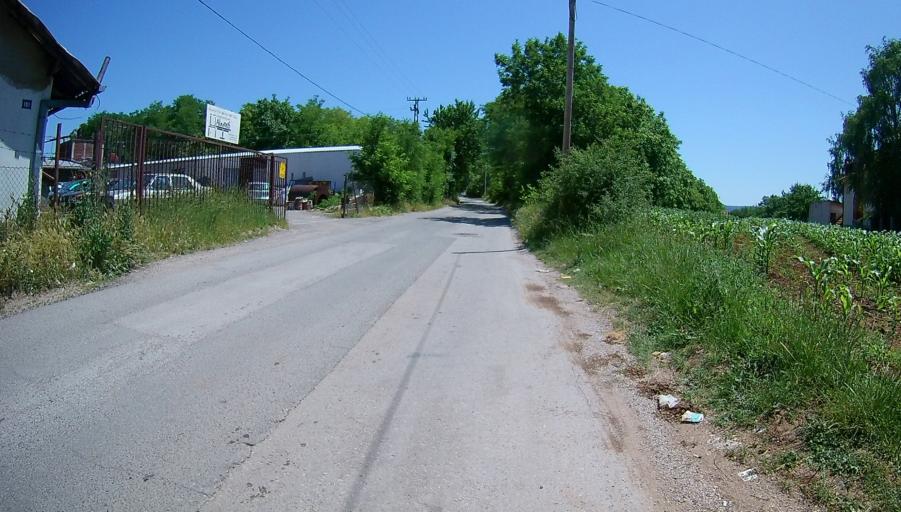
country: RS
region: Central Serbia
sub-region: Nisavski Okrug
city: Nis
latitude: 43.2957
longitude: 21.8981
